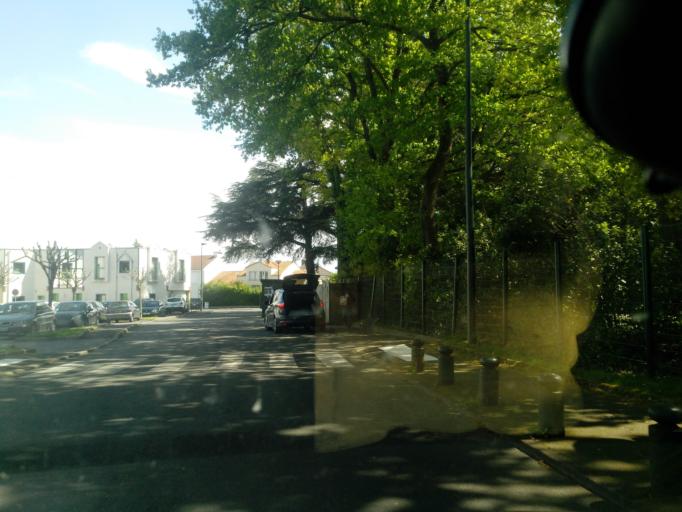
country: FR
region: Pays de la Loire
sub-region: Departement de la Loire-Atlantique
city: Orvault
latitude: 47.2525
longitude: -1.5956
